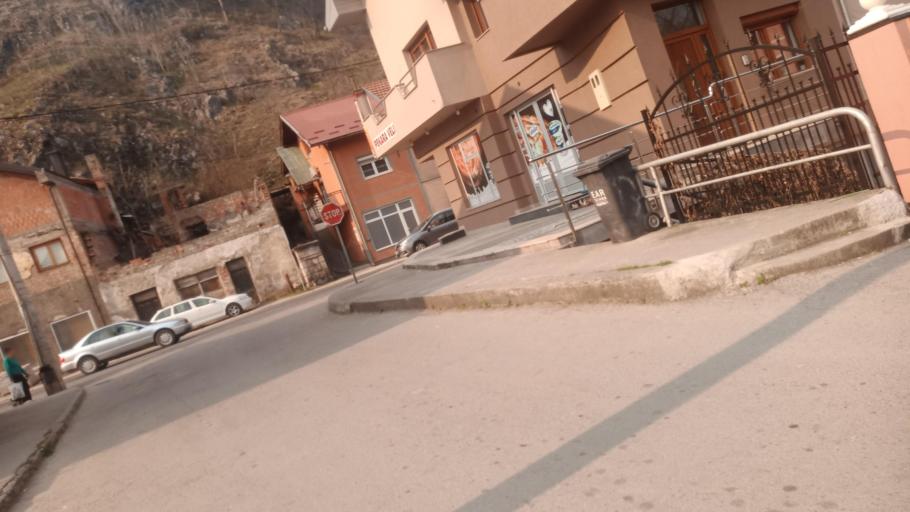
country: BA
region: Federation of Bosnia and Herzegovina
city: Bosanska Krupa
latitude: 44.8868
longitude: 16.1527
